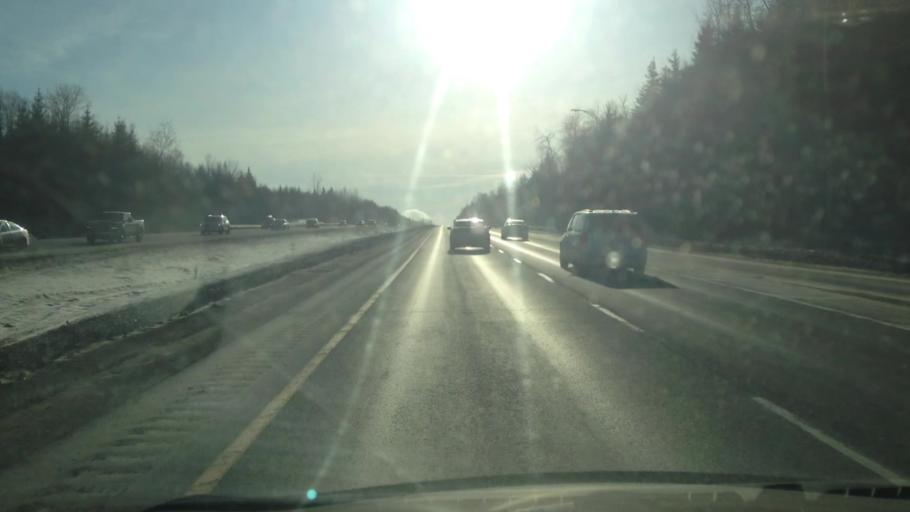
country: CA
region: Quebec
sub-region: Laurentides
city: Prevost
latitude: 45.8637
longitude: -74.0841
